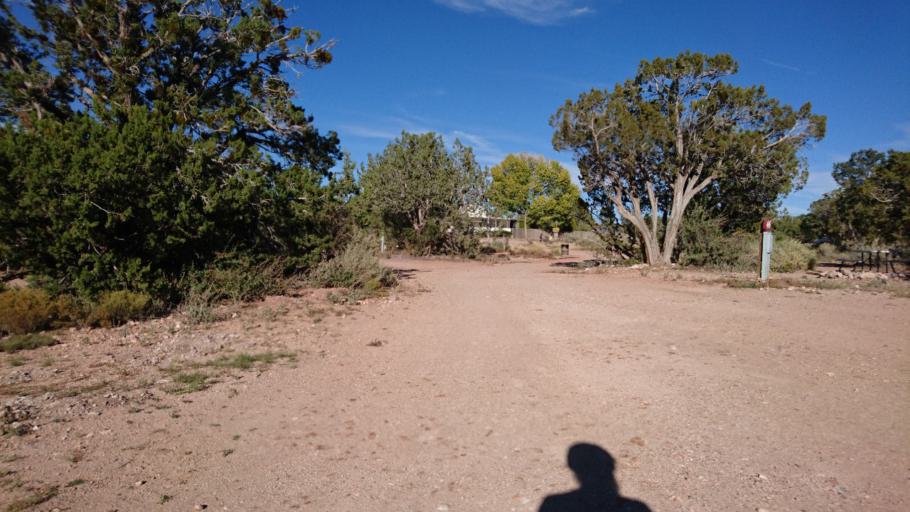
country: US
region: Arizona
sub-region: Mohave County
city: Peach Springs
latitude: 35.5169
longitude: -113.2198
